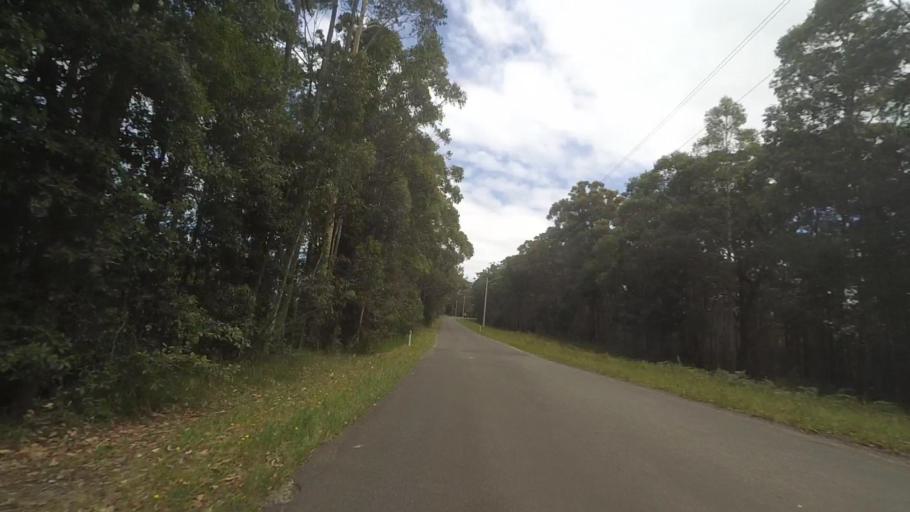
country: AU
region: New South Wales
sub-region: Shoalhaven Shire
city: Milton
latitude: -35.3799
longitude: 150.3731
